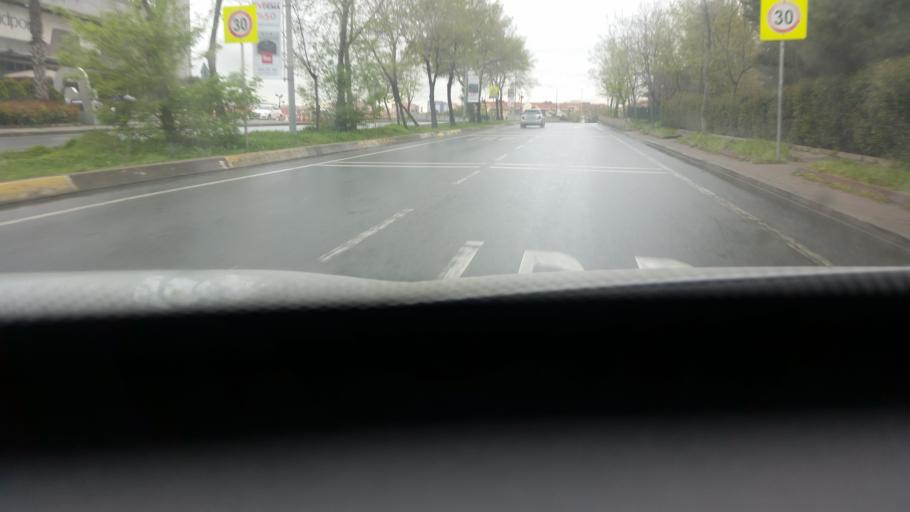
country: TR
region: Istanbul
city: Bahcelievler
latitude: 40.9787
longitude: 28.8512
